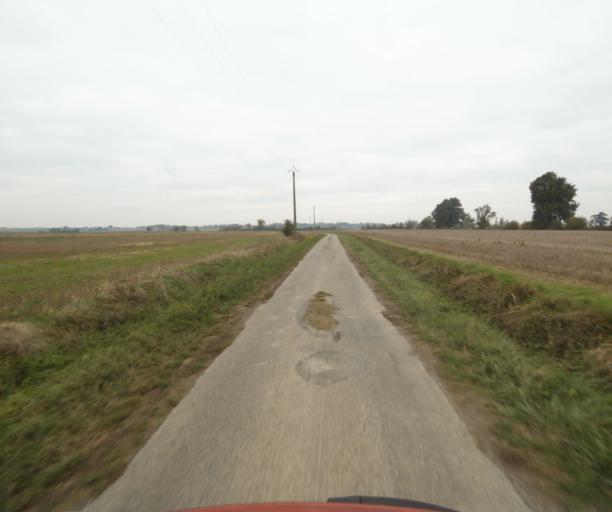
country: FR
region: Midi-Pyrenees
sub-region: Departement du Tarn-et-Garonne
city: Verdun-sur-Garonne
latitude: 43.8147
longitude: 1.2285
